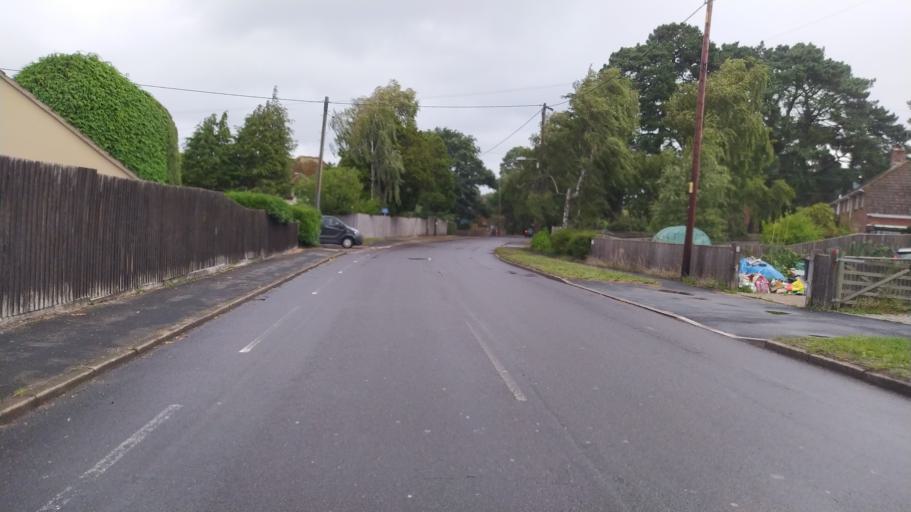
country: GB
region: England
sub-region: Dorset
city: St Leonards
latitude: 50.8308
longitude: -1.8378
